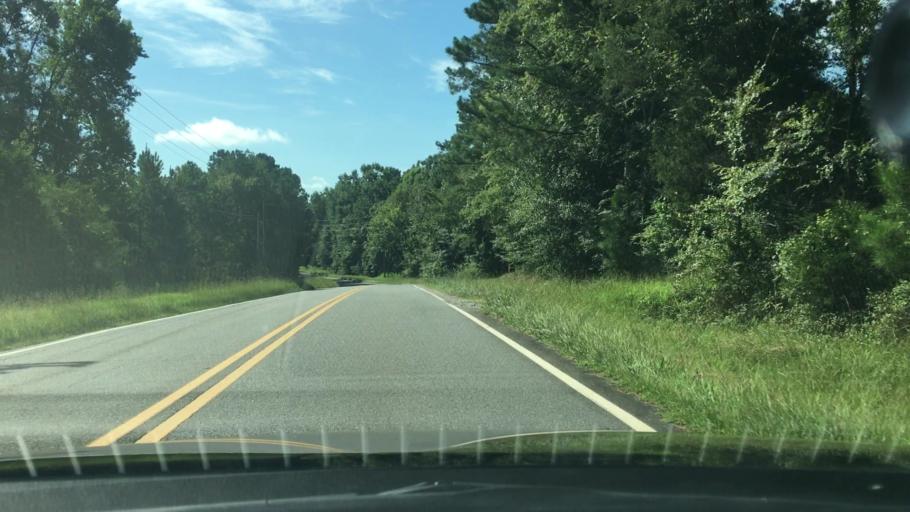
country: US
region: Georgia
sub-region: Putnam County
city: Jefferson
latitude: 33.4456
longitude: -83.2934
